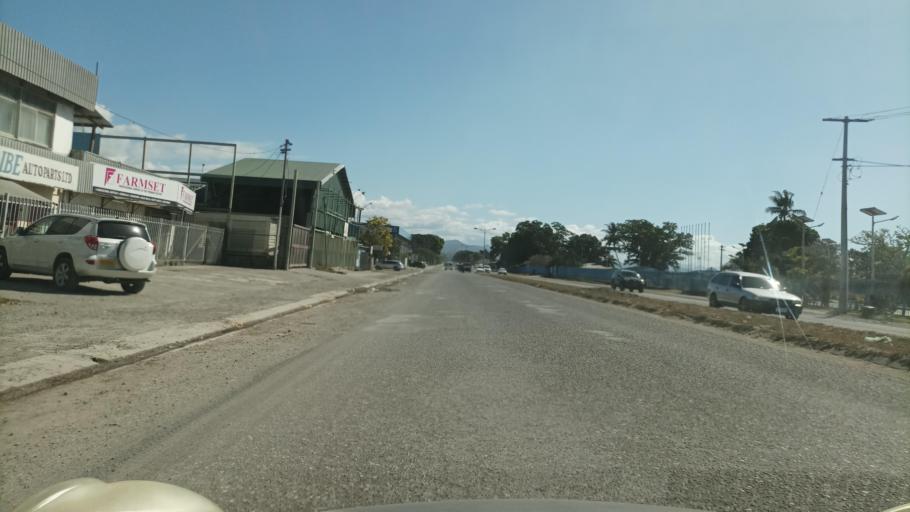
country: SB
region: Guadalcanal
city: Honiara
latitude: -9.4293
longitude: 160.0016
